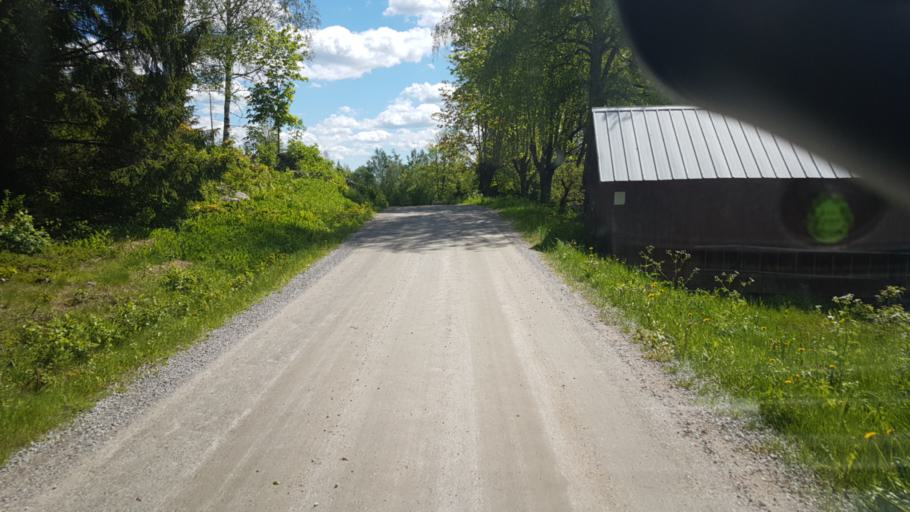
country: SE
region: Vaermland
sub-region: Sunne Kommun
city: Sunne
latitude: 59.7083
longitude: 12.8784
